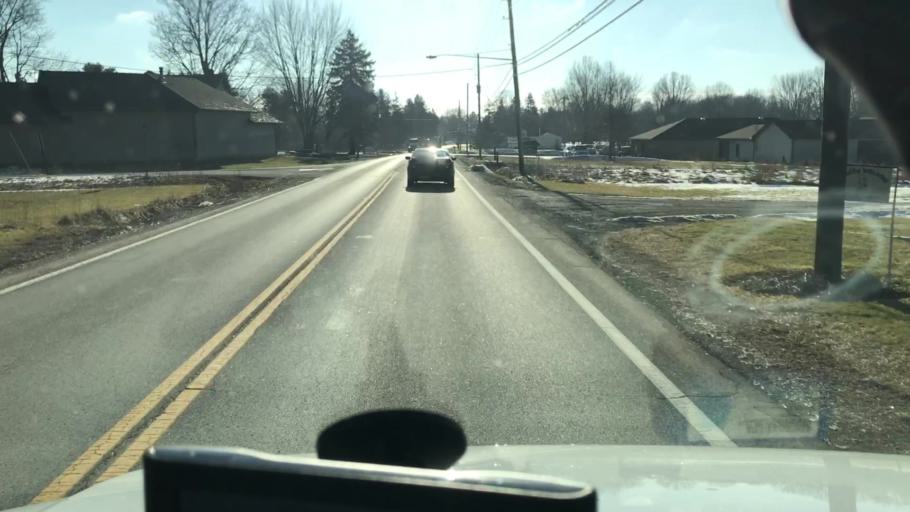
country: US
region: Ohio
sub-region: Mahoning County
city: New Middletown
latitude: 40.9238
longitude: -80.6152
